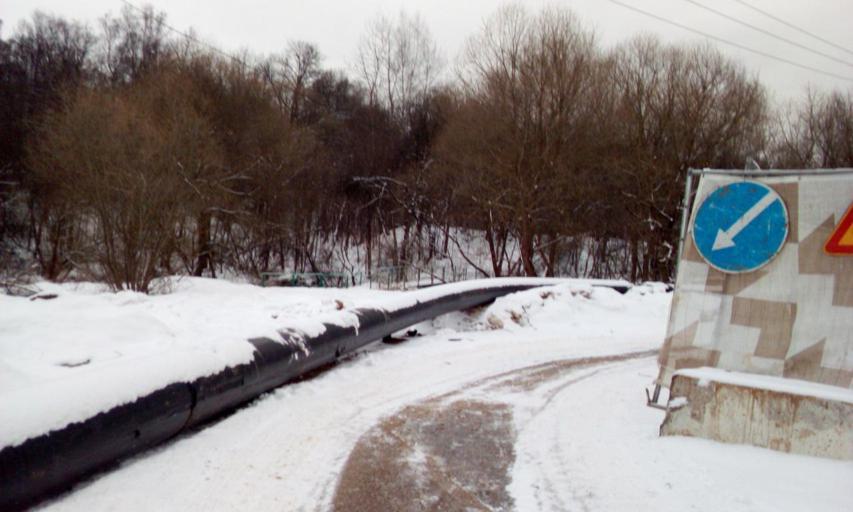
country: RU
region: Moskovskaya
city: Moskovskiy
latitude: 55.5938
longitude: 37.3278
